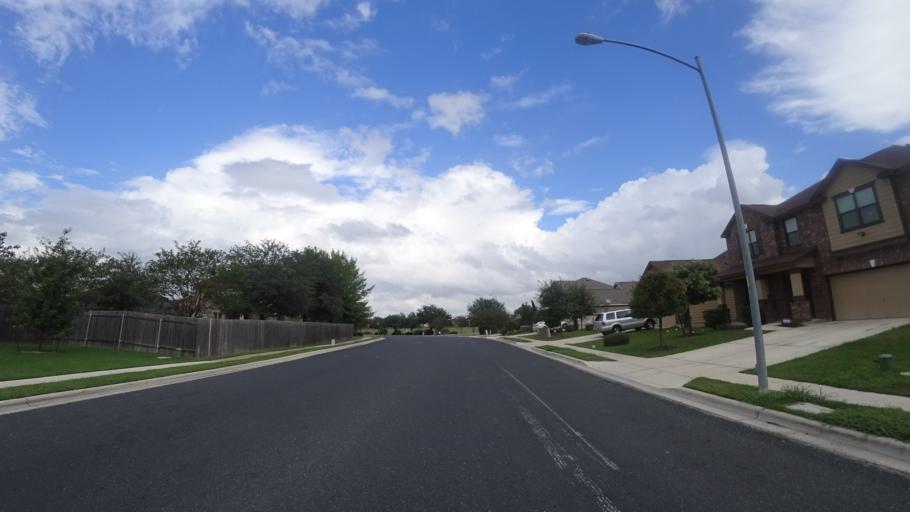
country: US
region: Texas
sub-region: Travis County
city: Onion Creek
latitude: 30.1552
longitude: -97.7439
